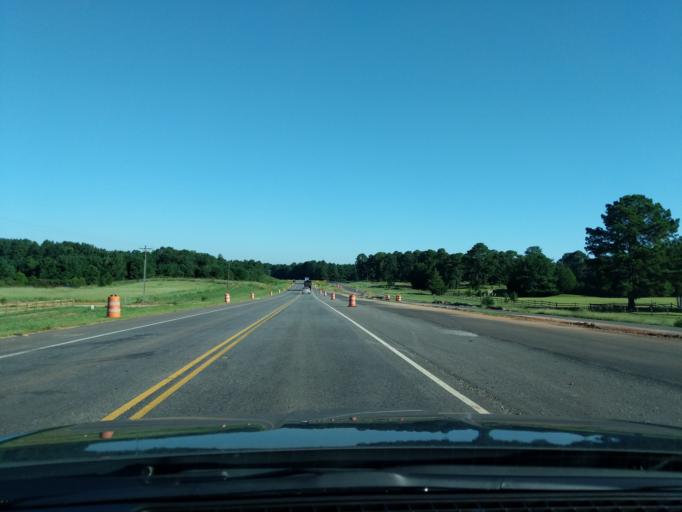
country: US
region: Georgia
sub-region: McDuffie County
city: Thomson
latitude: 33.5689
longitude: -82.5185
